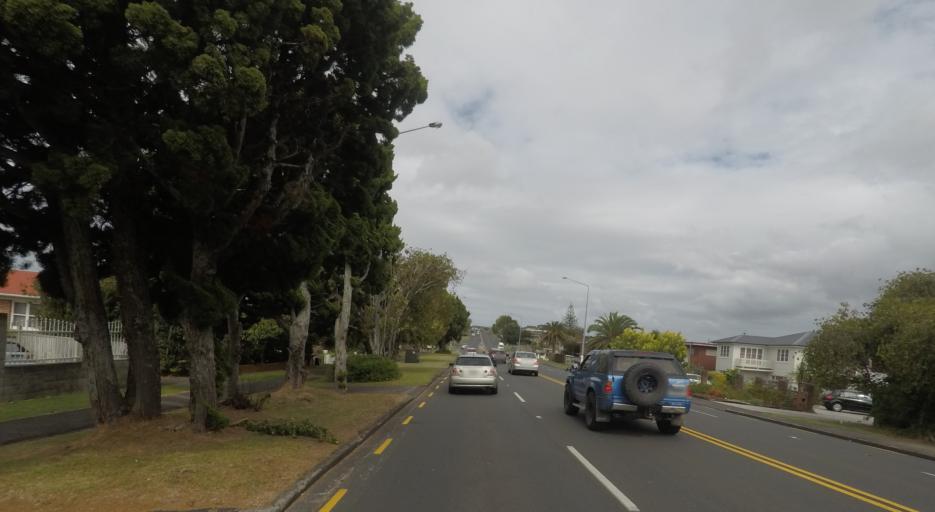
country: NZ
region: Auckland
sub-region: Auckland
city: Rosebank
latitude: -36.8886
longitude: 174.6446
